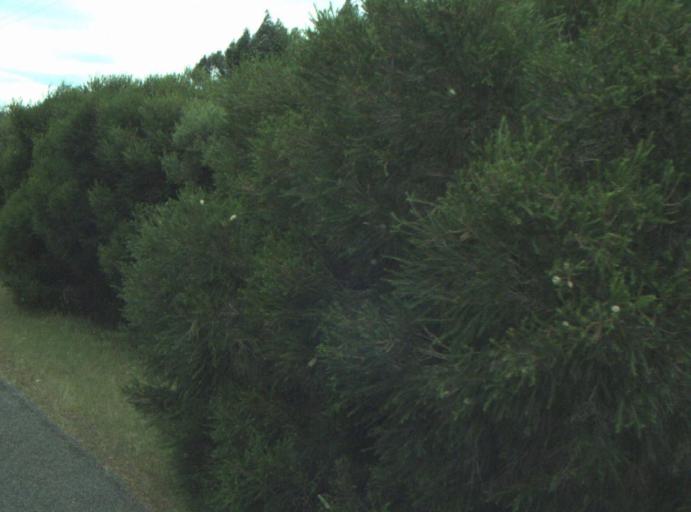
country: AU
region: Victoria
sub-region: Greater Geelong
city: Leopold
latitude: -38.2157
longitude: 144.4496
